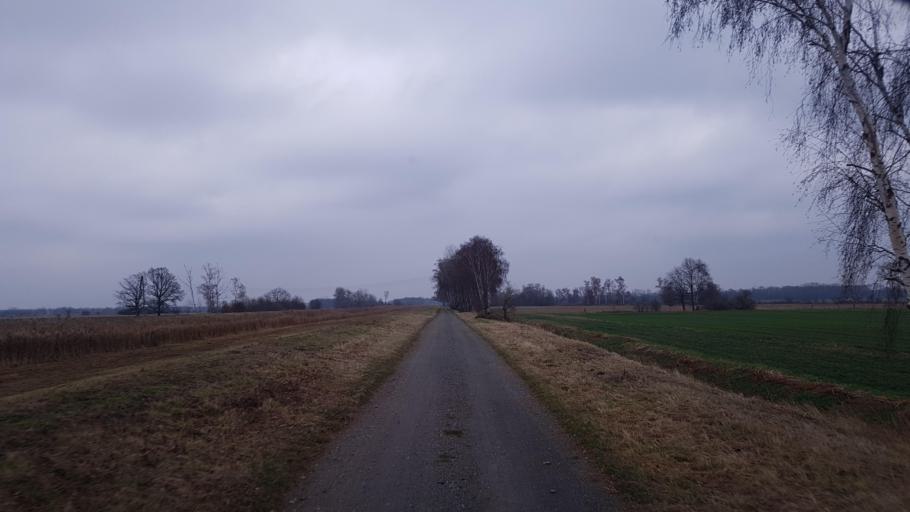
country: DE
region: Brandenburg
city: Schraden
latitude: 51.4608
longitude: 13.6811
